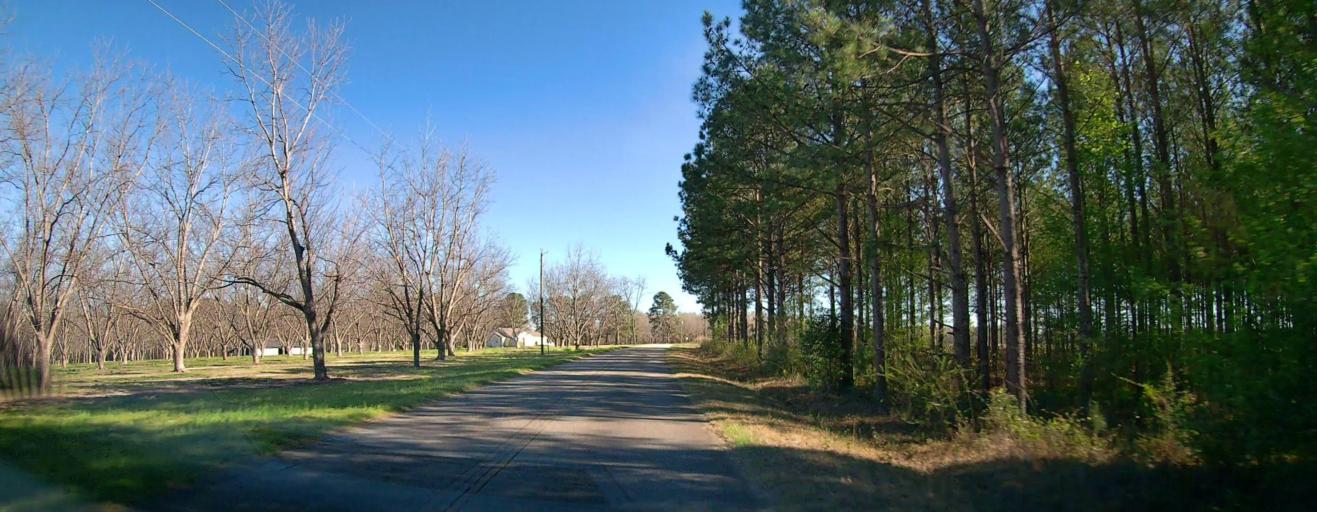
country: US
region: Georgia
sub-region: Peach County
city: Fort Valley
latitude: 32.6347
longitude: -83.8555
